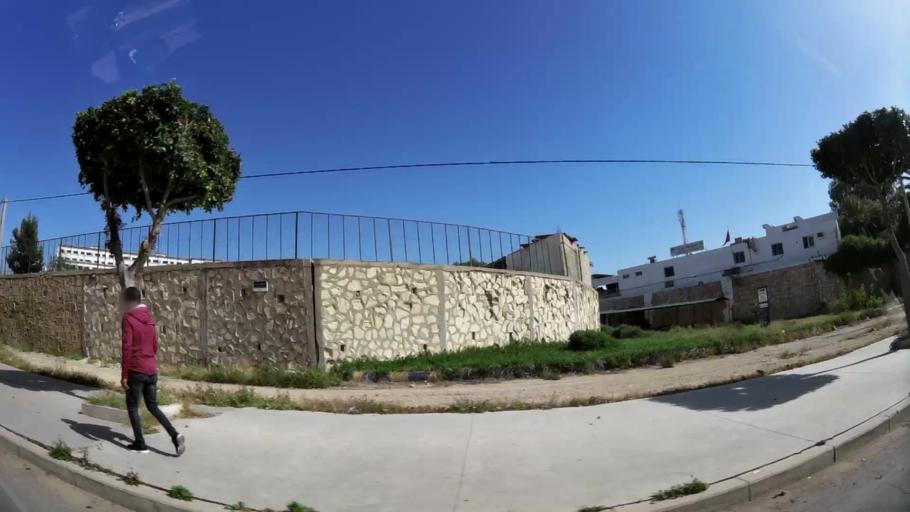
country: MA
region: Souss-Massa-Draa
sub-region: Agadir-Ida-ou-Tnan
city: Agadir
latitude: 30.4201
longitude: -9.5876
